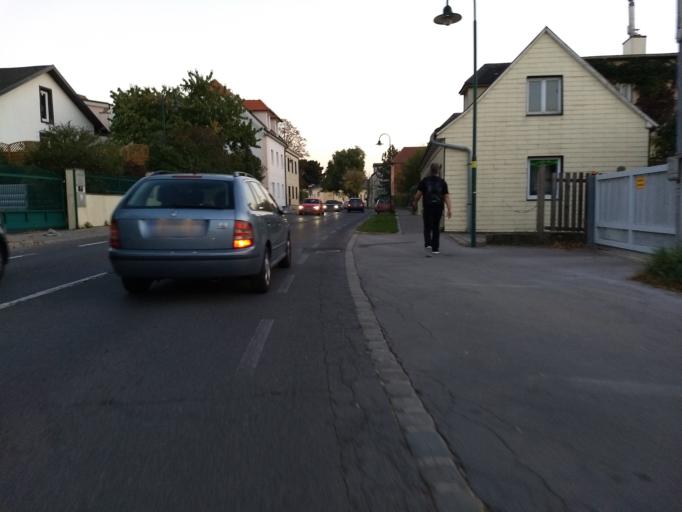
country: AT
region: Lower Austria
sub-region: Politischer Bezirk Modling
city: Perchtoldsdorf
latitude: 48.1153
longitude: 16.2722
